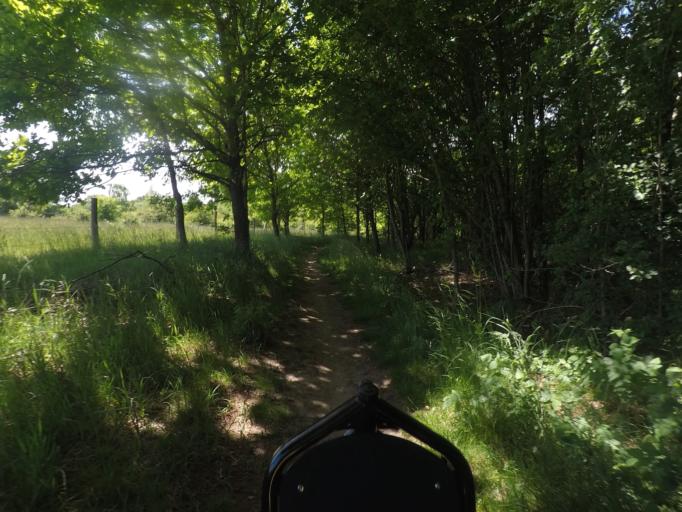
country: DE
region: Schleswig-Holstein
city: Stapelfeld
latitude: 53.6255
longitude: 10.2181
